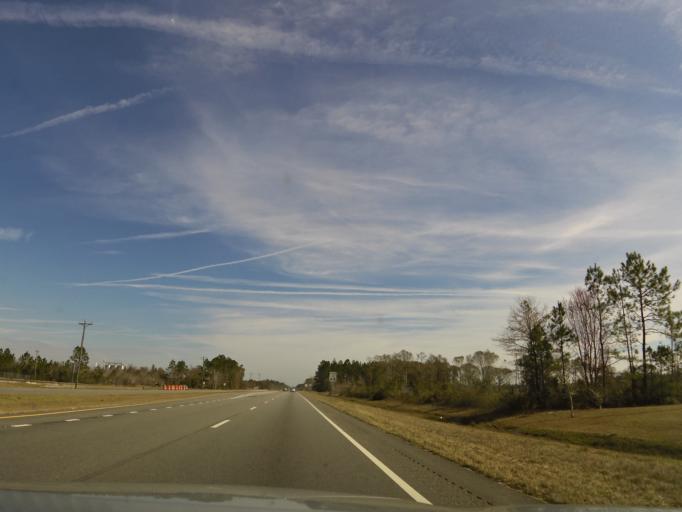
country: US
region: Georgia
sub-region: Brantley County
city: Nahunta
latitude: 31.2069
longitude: -81.9612
